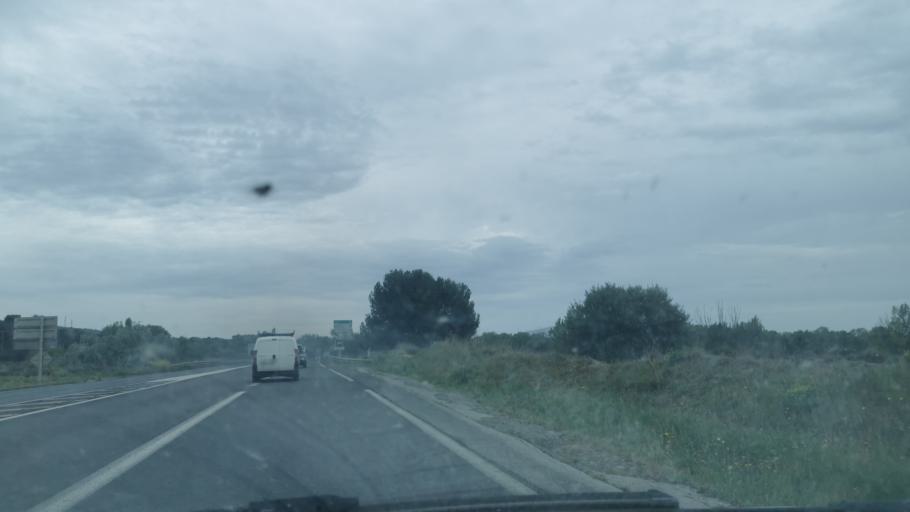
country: FR
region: Languedoc-Roussillon
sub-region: Departement de l'Herault
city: Balaruc-le-Vieux
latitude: 43.4744
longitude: 3.6865
